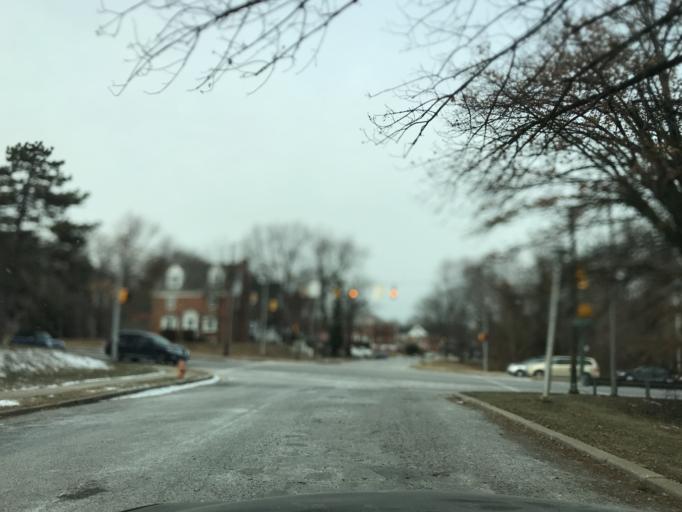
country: US
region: Maryland
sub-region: Baltimore County
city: Towson
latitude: 39.3650
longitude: -76.5996
